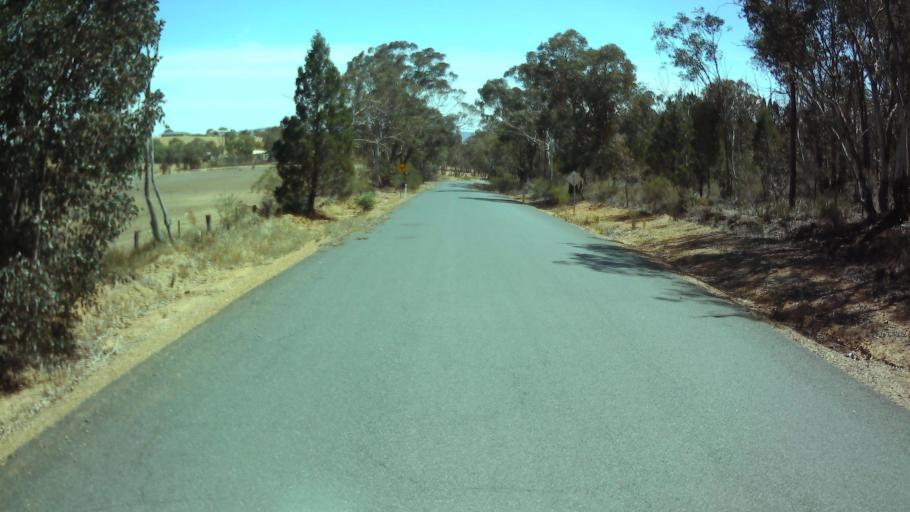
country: AU
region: New South Wales
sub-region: Weddin
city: Grenfell
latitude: -33.9068
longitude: 148.1809
